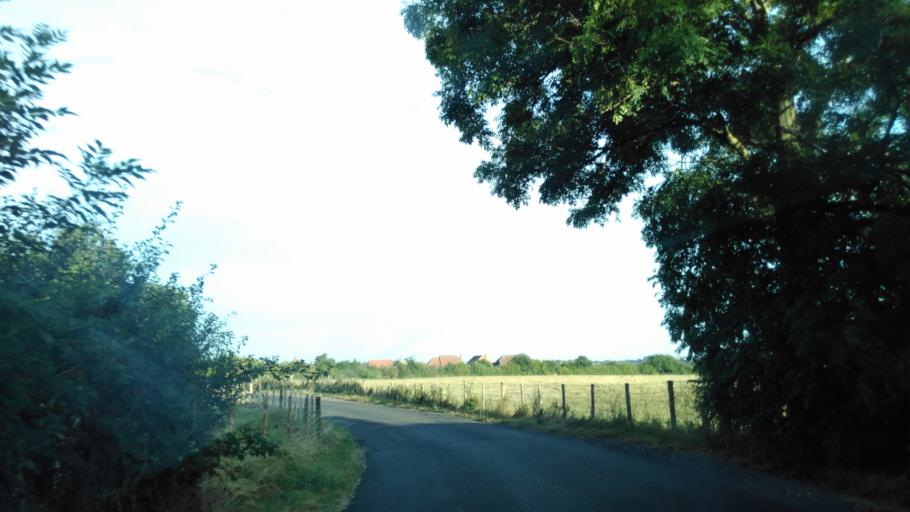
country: GB
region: England
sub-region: Kent
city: Dunkirk
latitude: 51.3138
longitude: 0.9957
